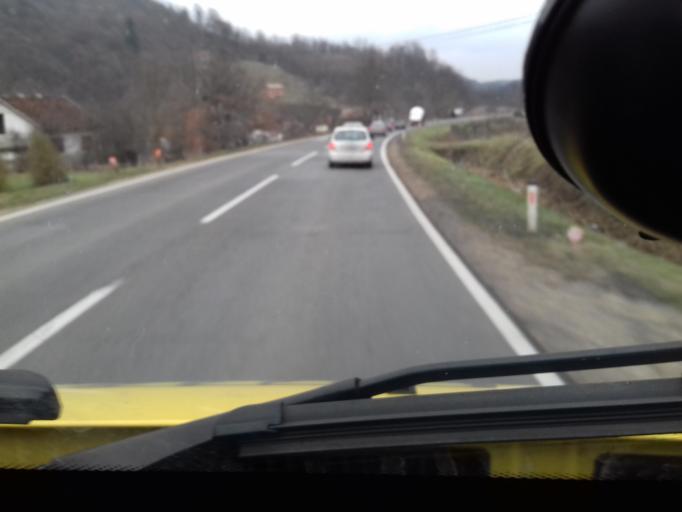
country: BA
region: Federation of Bosnia and Herzegovina
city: Lijesnica
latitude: 44.5024
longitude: 18.0794
